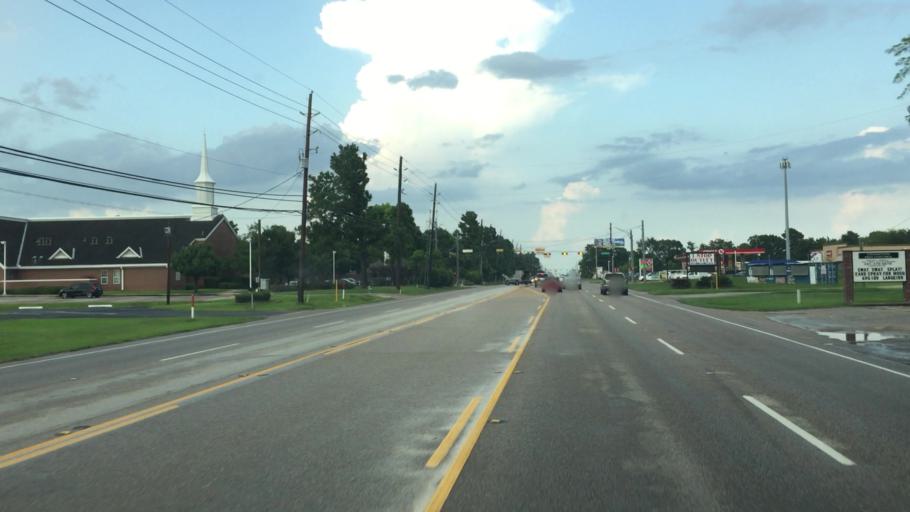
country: US
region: Texas
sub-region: Harris County
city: Spring
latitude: 30.0318
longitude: -95.5042
